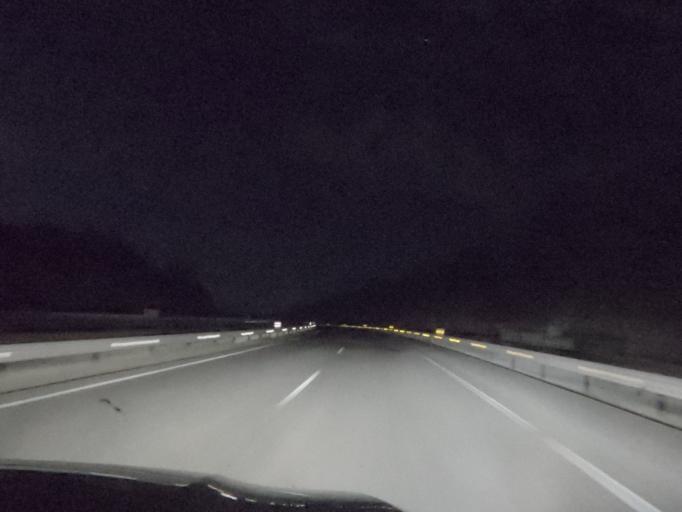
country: ES
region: Galicia
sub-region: Provincia de Ourense
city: Xinzo de Limia
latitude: 42.0696
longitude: -7.7053
